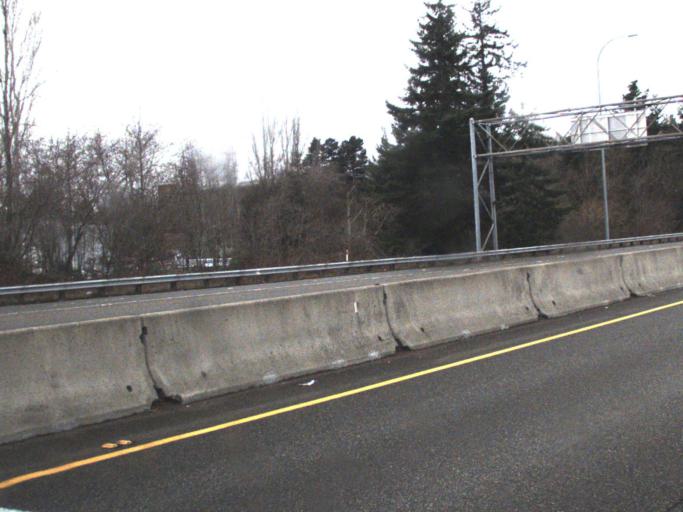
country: US
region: Washington
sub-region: Snohomish County
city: Mukilteo
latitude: 47.9223
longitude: -122.2643
